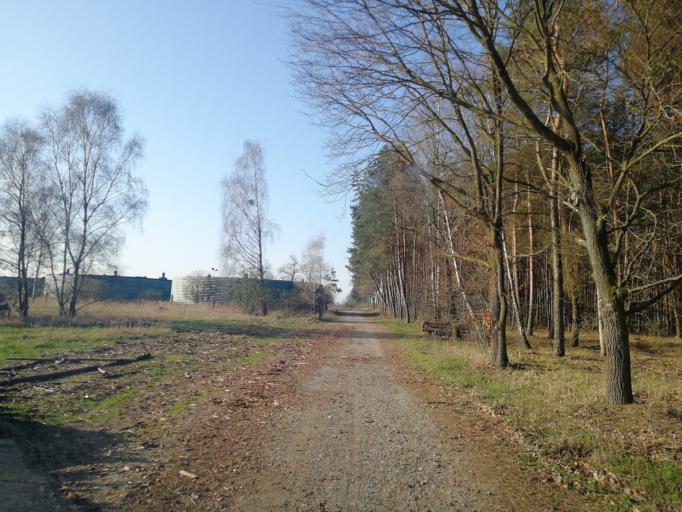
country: DE
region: Brandenburg
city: Drahnsdorf
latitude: 51.9261
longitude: 13.5803
